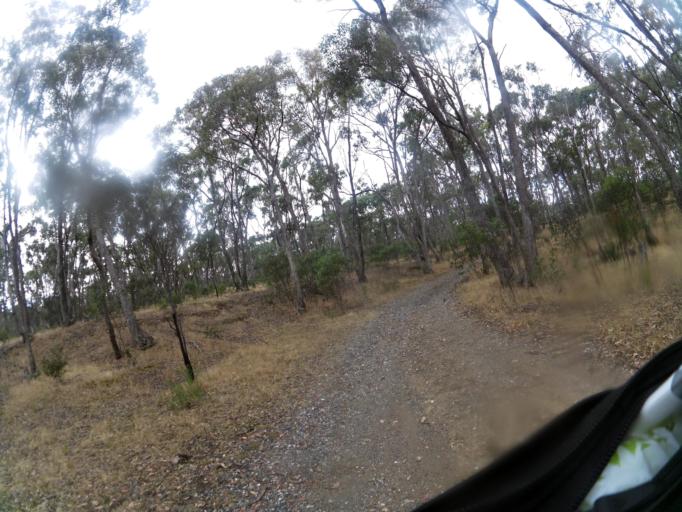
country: AU
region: Victoria
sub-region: Mount Alexander
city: Castlemaine
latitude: -37.0711
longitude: 144.2588
